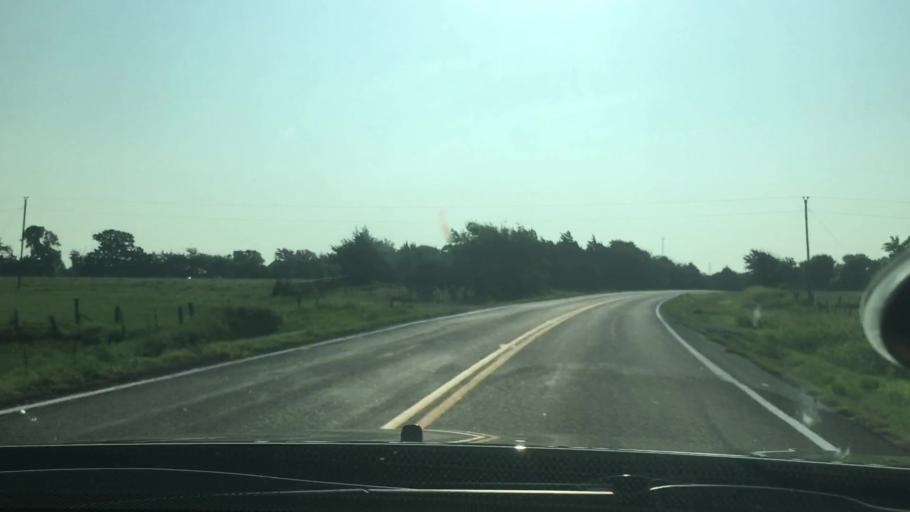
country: US
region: Oklahoma
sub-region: Bryan County
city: Durant
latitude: 34.1425
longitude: -96.2852
